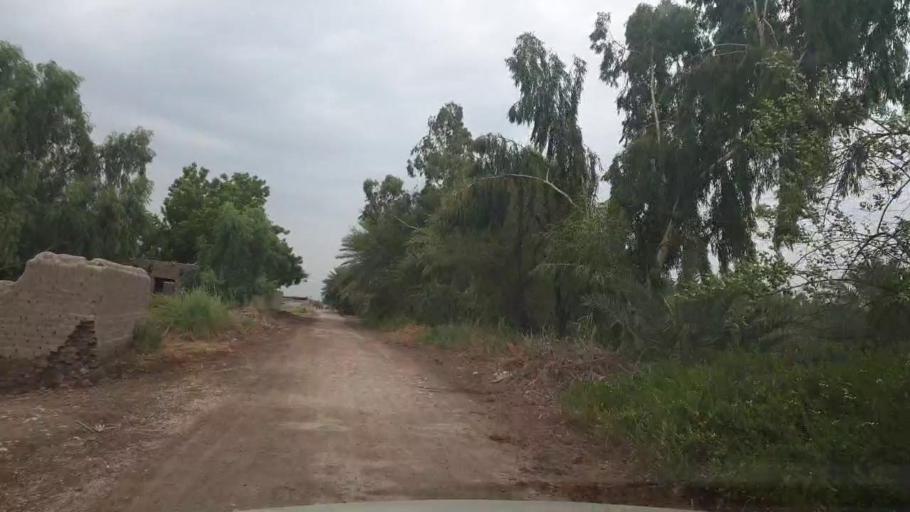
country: PK
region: Sindh
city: Khairpur
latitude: 27.5924
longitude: 68.8136
